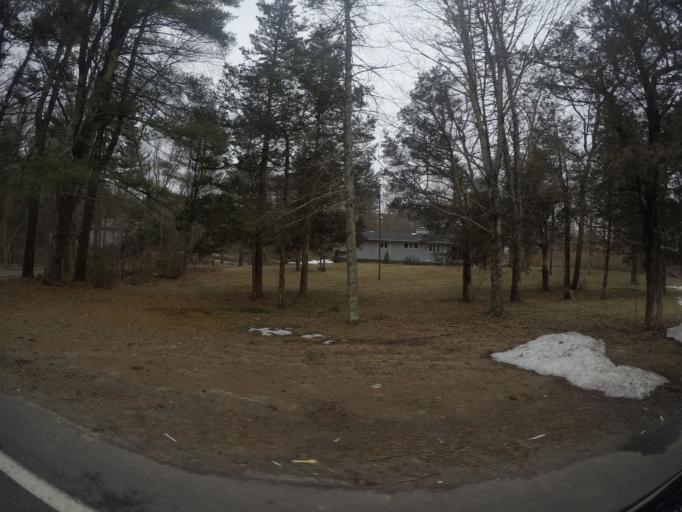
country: US
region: Massachusetts
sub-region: Bristol County
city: Easton
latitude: 42.0165
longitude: -71.0929
